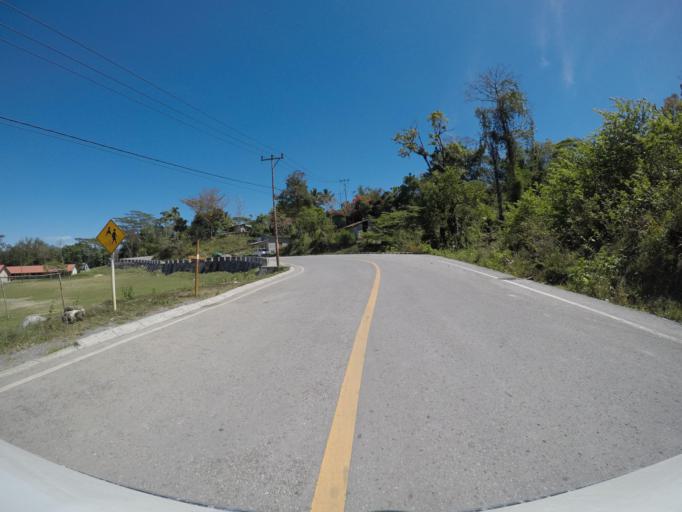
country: TL
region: Manatuto
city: Manatuto
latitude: -8.8276
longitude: 125.9860
